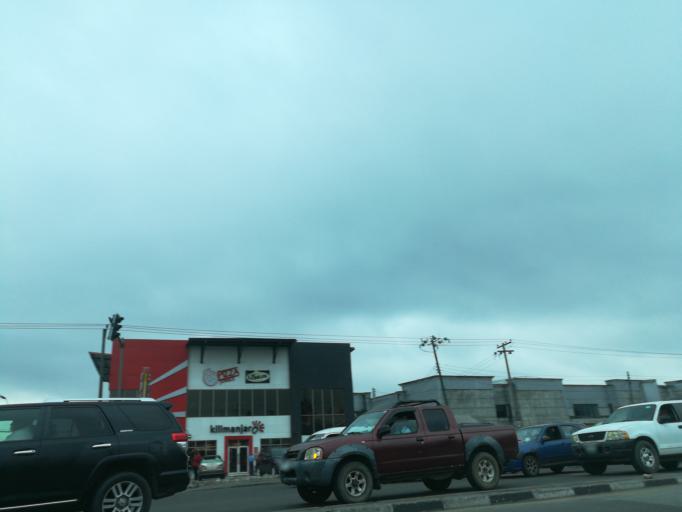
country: NG
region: Rivers
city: Port Harcourt
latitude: 4.8242
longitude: 7.0060
